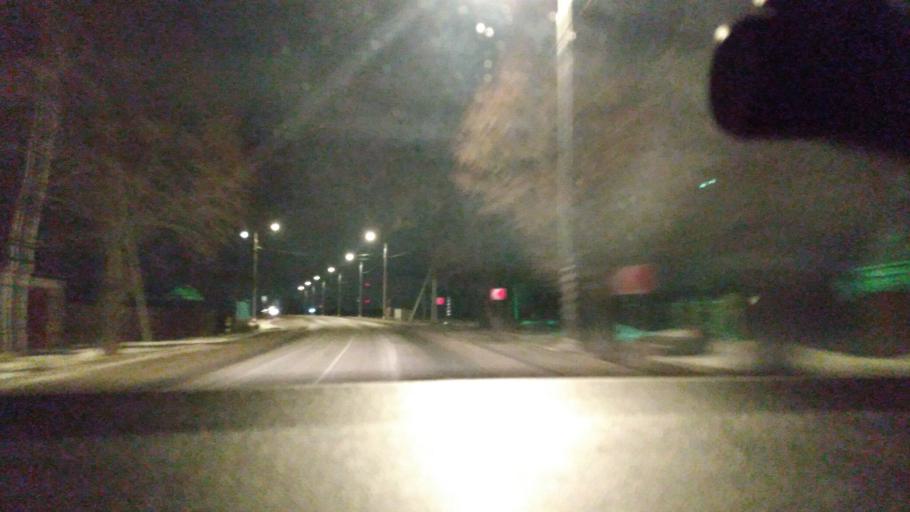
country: RU
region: Moskovskaya
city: Krasnaya Poyma
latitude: 55.1114
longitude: 39.0282
